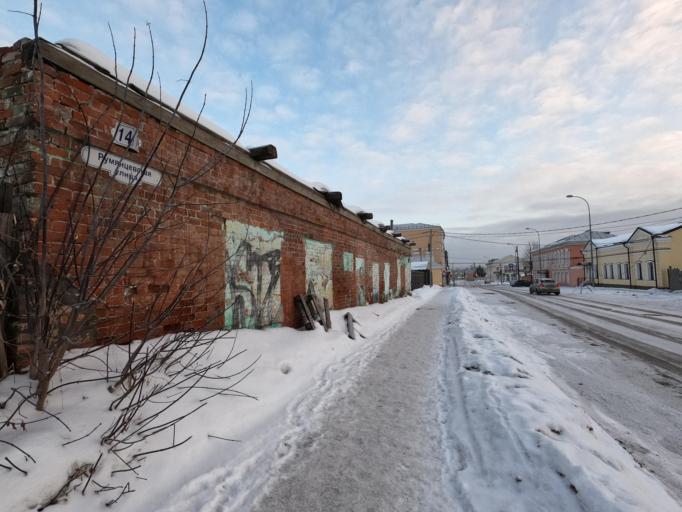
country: RU
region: Jaroslavl
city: Rybinsk
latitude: 58.0494
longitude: 38.8452
